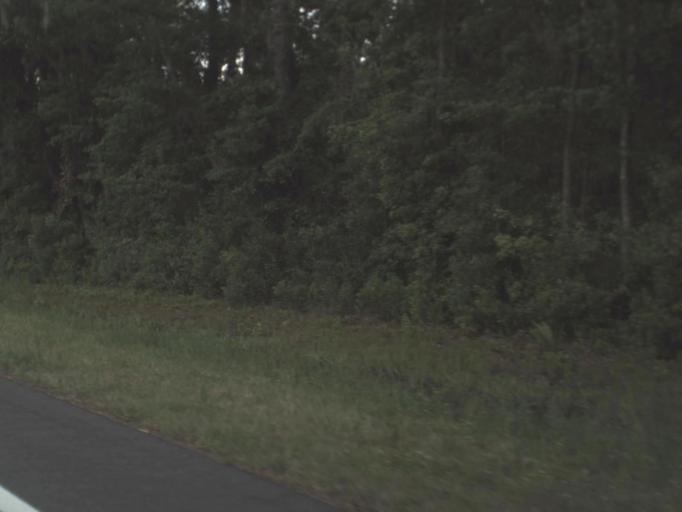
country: US
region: Florida
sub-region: Columbia County
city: Five Points
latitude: 30.4493
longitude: -82.6483
